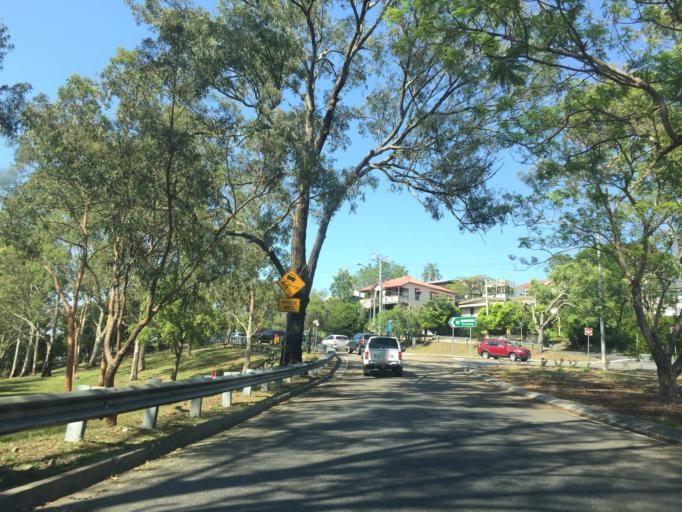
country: AU
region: Queensland
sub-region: Brisbane
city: Milton
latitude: -27.4651
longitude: 152.9887
